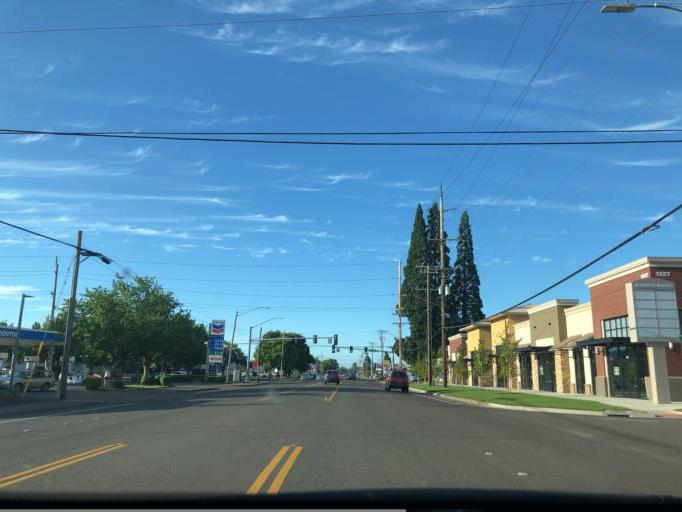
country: US
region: Oregon
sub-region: Benton County
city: Corvallis
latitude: 44.5786
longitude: -123.2605
